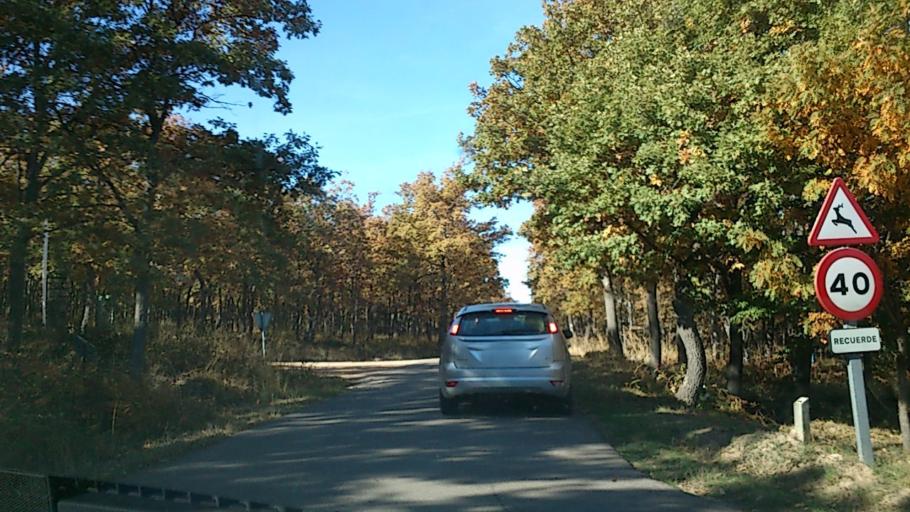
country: ES
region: Aragon
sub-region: Provincia de Zaragoza
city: Lituenigo
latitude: 41.8094
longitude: -1.8034
